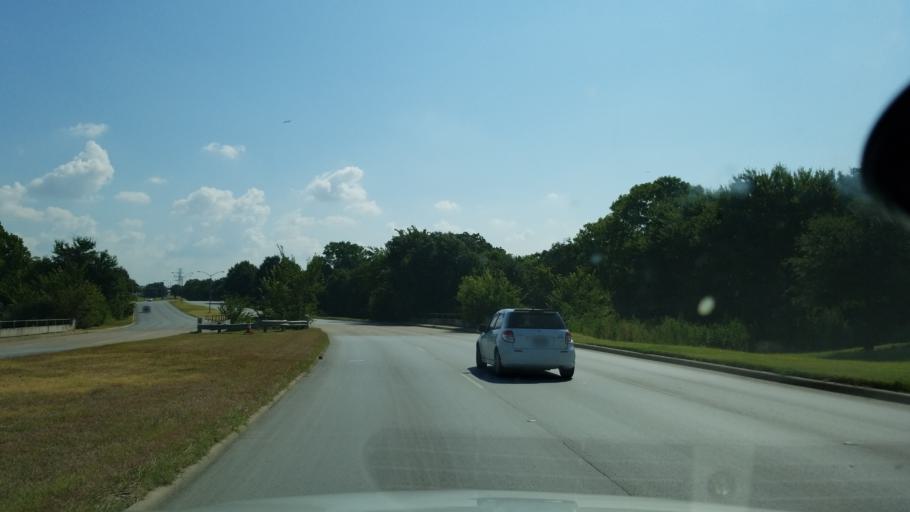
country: US
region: Texas
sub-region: Tarrant County
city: Euless
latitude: 32.8168
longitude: -97.0932
